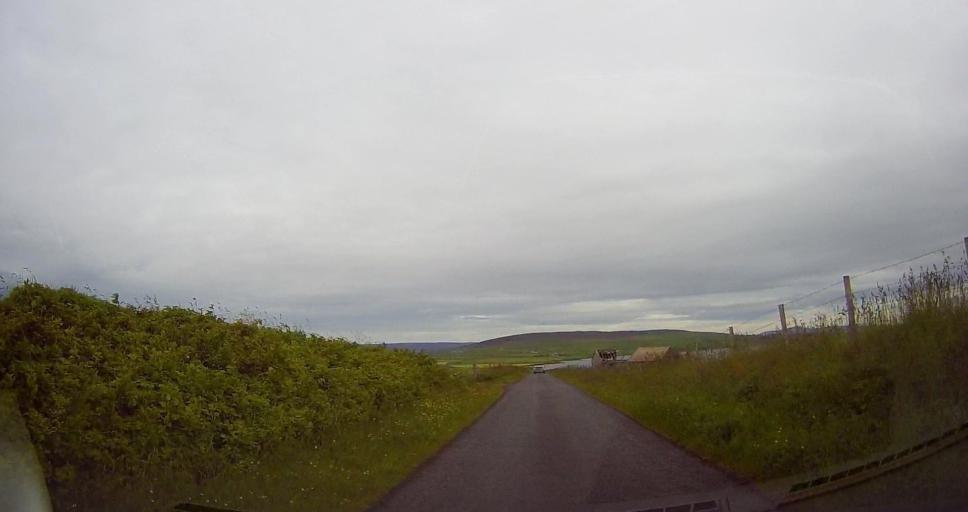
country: GB
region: Scotland
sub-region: Orkney Islands
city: Stromness
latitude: 59.1214
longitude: -3.2759
